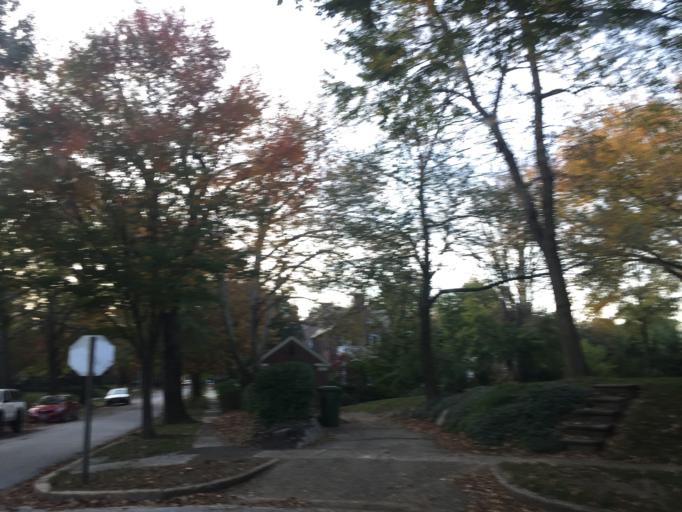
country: US
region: Maryland
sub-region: City of Baltimore
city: Baltimore
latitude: 39.3419
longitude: -76.6319
